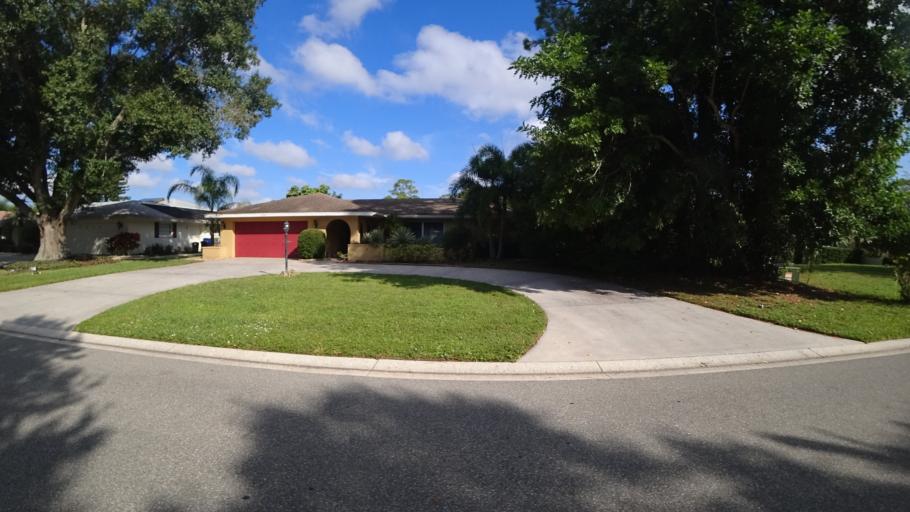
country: US
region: Florida
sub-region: Sarasota County
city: Desoto Lakes
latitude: 27.3994
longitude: -82.4927
